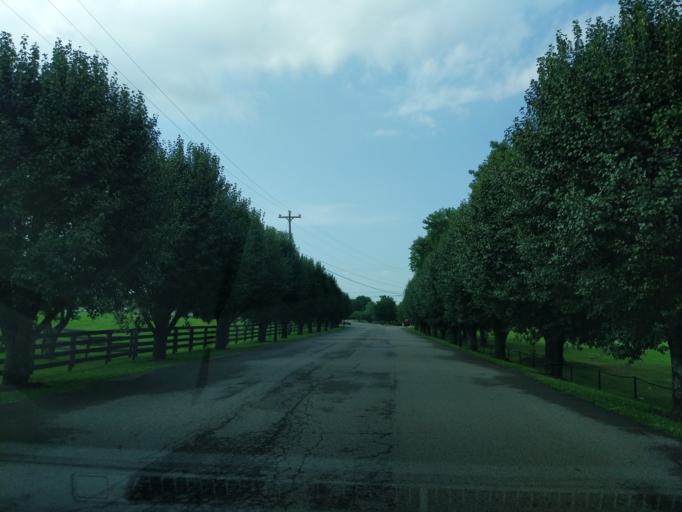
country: US
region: Tennessee
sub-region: Cheatham County
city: Pegram
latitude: 36.0298
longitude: -86.9591
